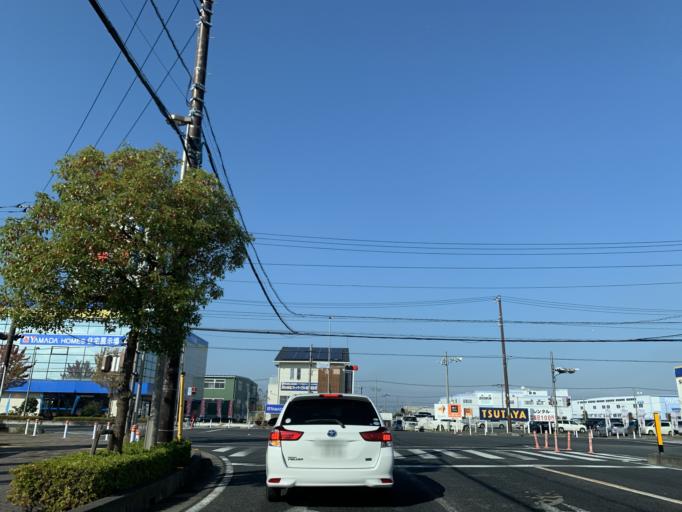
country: JP
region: Saitama
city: Yashio-shi
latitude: 35.8456
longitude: 139.8550
